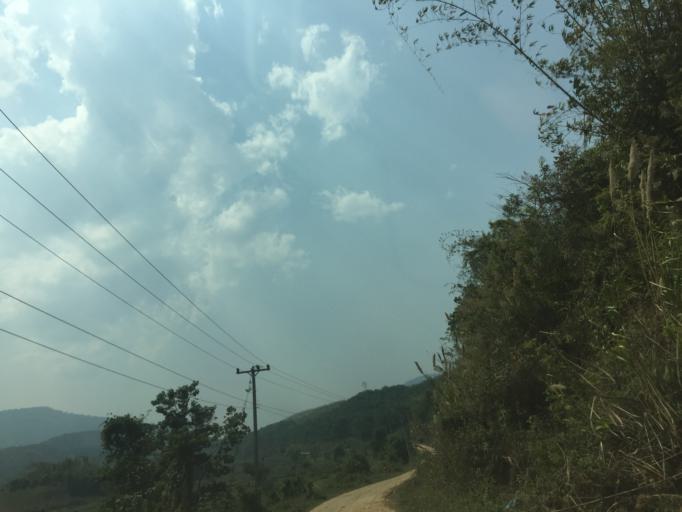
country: TH
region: Nan
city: Thung Chang
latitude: 19.7295
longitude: 100.7425
